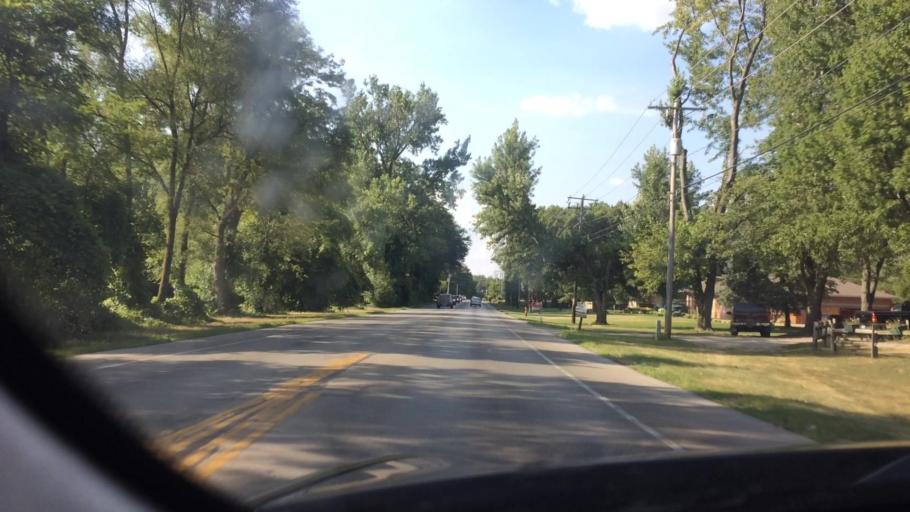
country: US
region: Ohio
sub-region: Lucas County
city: Holland
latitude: 41.6478
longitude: -83.7036
